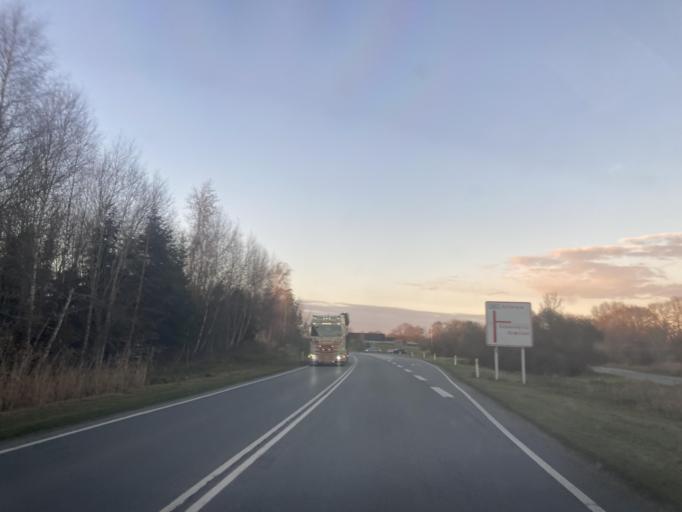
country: DK
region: Capital Region
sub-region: Gribskov Kommune
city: Graested
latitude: 56.0472
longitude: 12.2822
